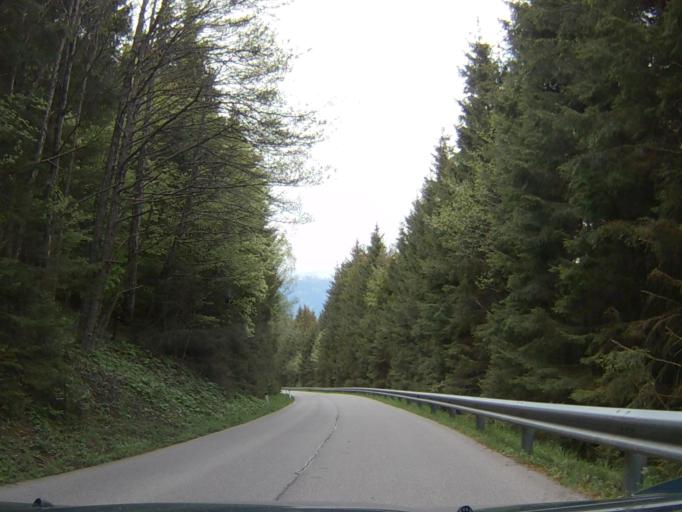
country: AT
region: Carinthia
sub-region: Politischer Bezirk Villach Land
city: Stockenboi
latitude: 46.7384
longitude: 13.5638
